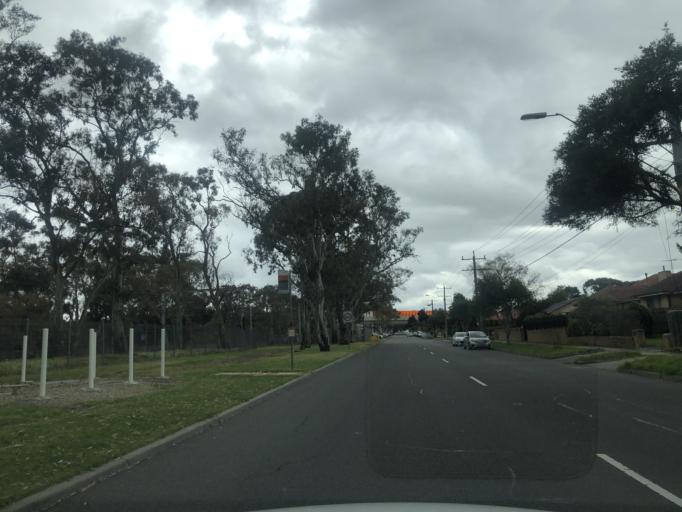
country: AU
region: Victoria
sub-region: Greater Dandenong
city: Dandenong
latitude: -37.9806
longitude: 145.1956
